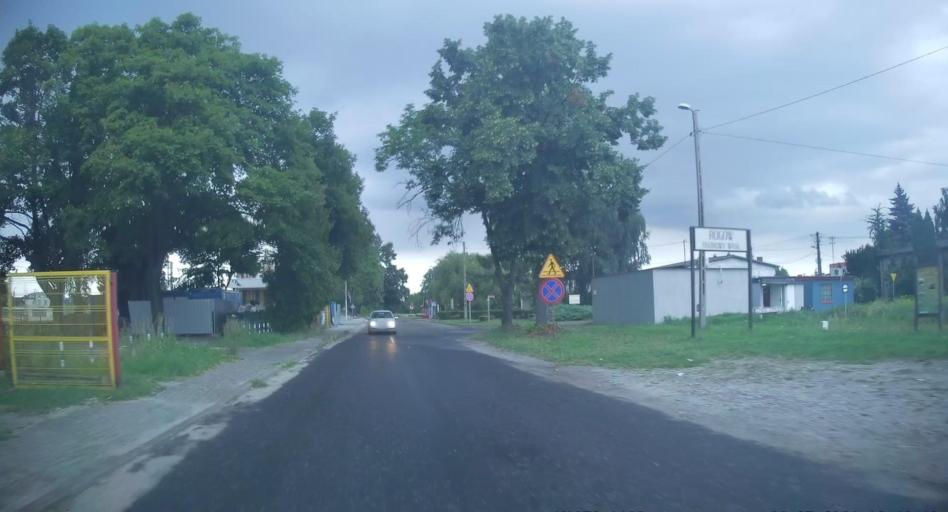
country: PL
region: Lodz Voivodeship
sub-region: Powiat brzezinski
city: Rogow
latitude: 51.8171
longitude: 19.8855
